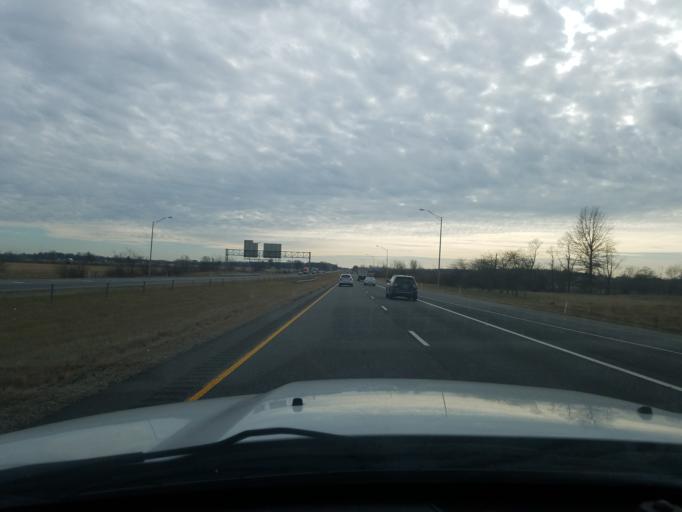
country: US
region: Indiana
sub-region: Madison County
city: Alexandria
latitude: 40.2747
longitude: -85.5581
